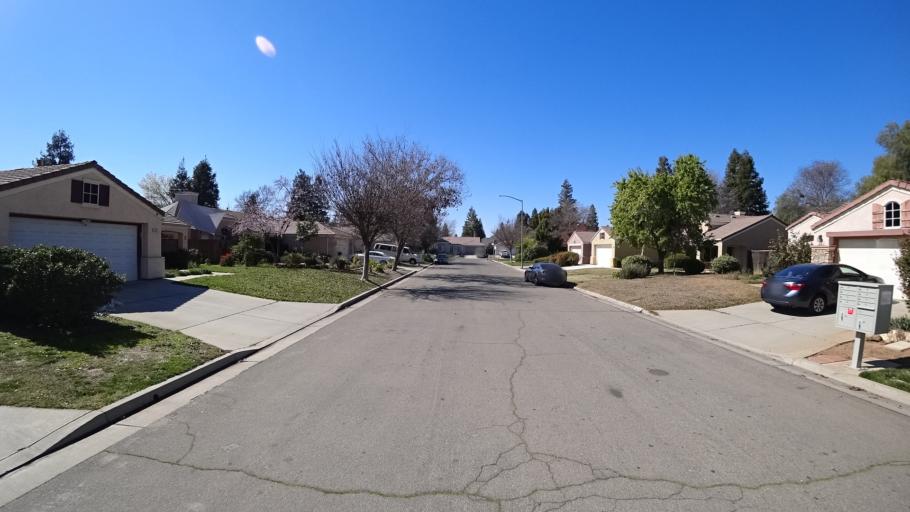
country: US
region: California
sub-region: Fresno County
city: Clovis
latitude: 36.8487
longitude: -119.7419
